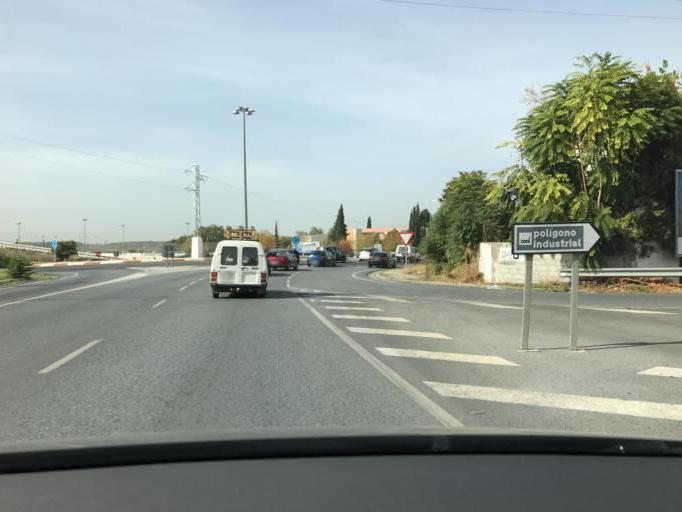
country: ES
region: Andalusia
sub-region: Provincia de Granada
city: Maracena
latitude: 37.1988
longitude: -3.6481
